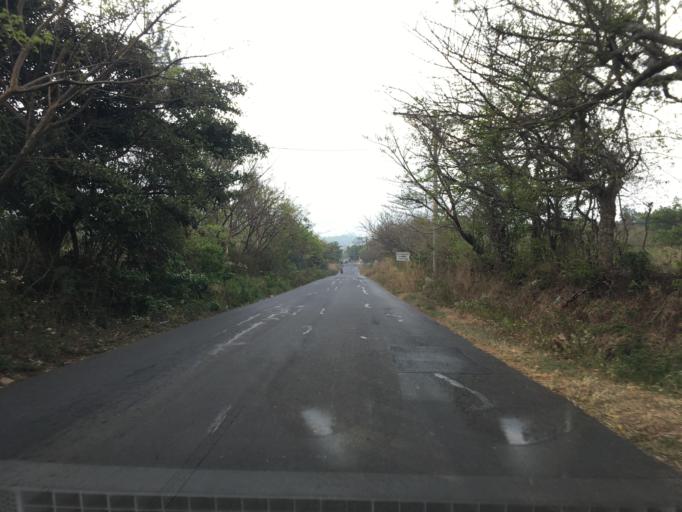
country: GT
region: Escuintla
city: San Vicente Pacaya
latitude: 14.3257
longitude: -90.5617
